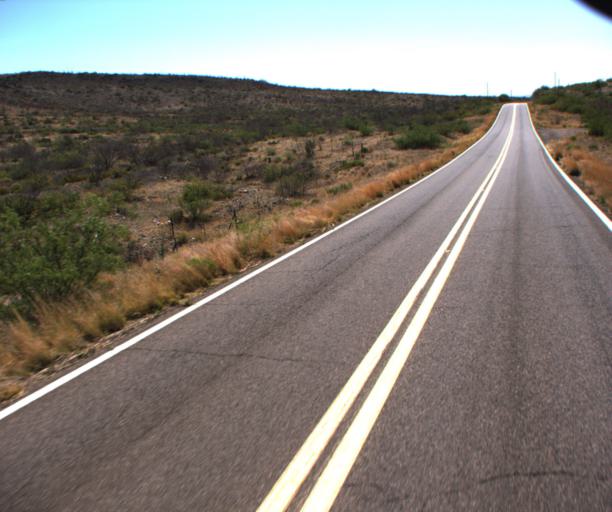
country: US
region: Arizona
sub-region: Cochise County
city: Douglas
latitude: 31.4710
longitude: -109.3878
